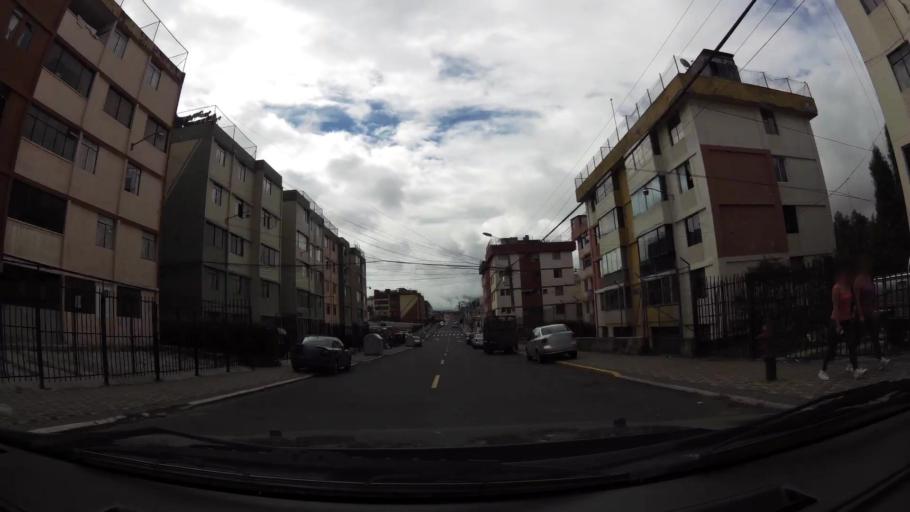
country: EC
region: Pichincha
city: Quito
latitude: -0.1329
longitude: -78.5009
